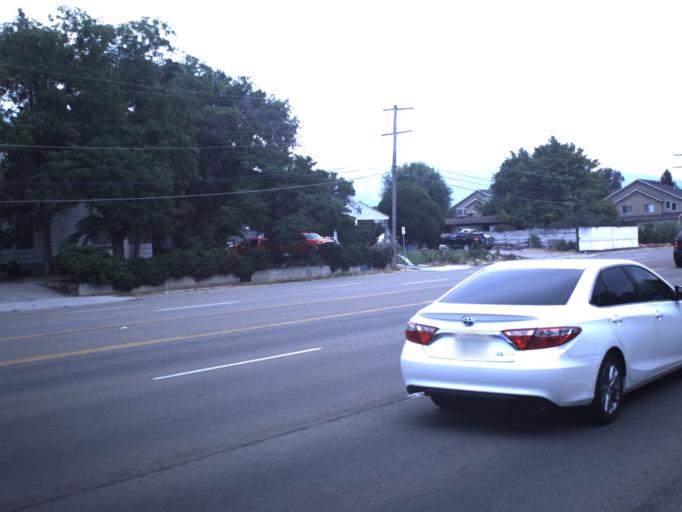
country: US
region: Utah
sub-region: Salt Lake County
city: Millcreek
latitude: 40.6830
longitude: -111.8716
